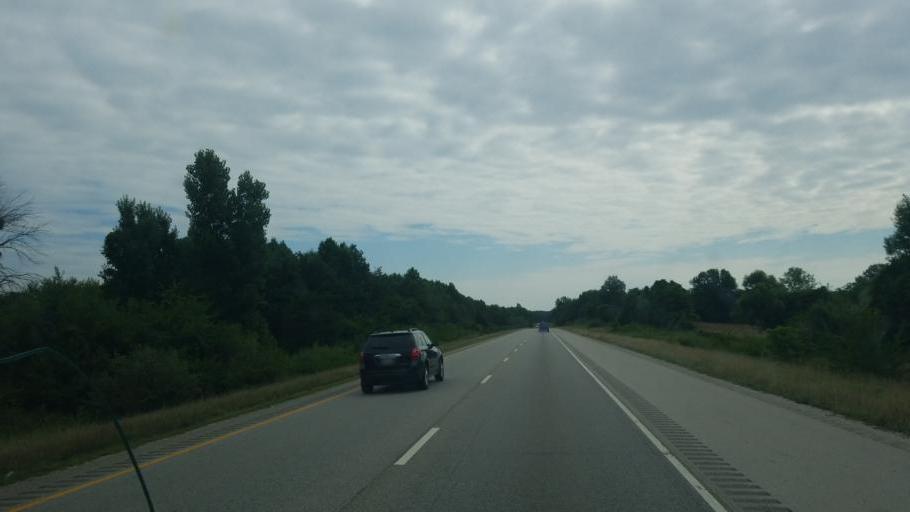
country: US
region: Indiana
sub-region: Vigo County
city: Seelyville
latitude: 39.4346
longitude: -87.2896
